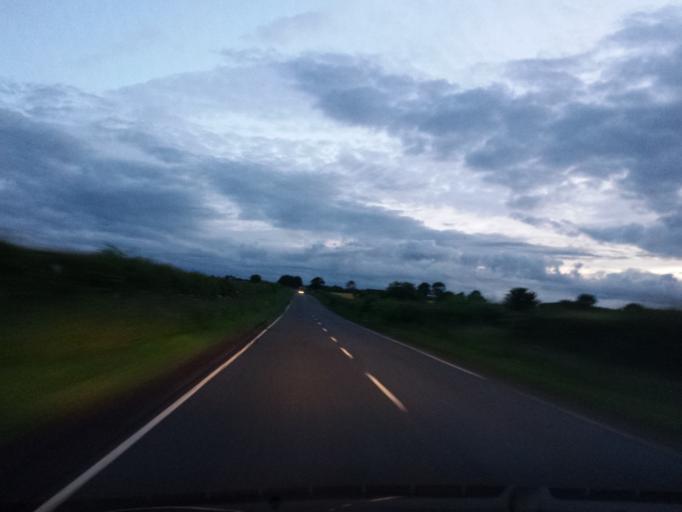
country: GB
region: Scotland
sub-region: The Scottish Borders
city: Duns
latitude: 55.7589
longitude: -2.3875
